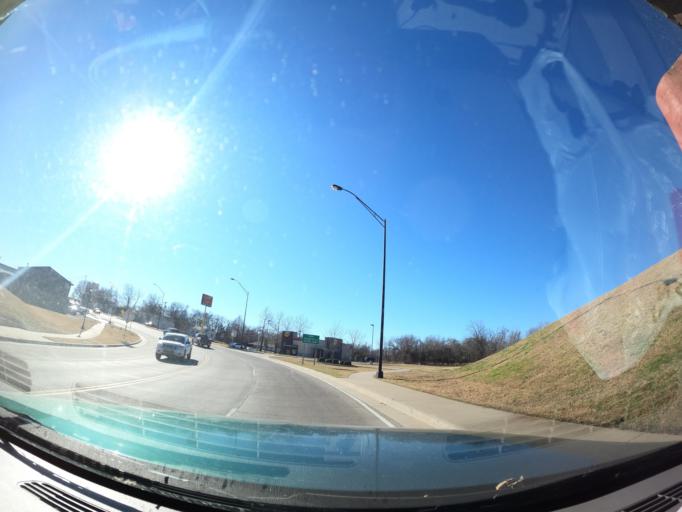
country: US
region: Oklahoma
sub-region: Wagoner County
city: Coweta
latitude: 35.9560
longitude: -95.6502
